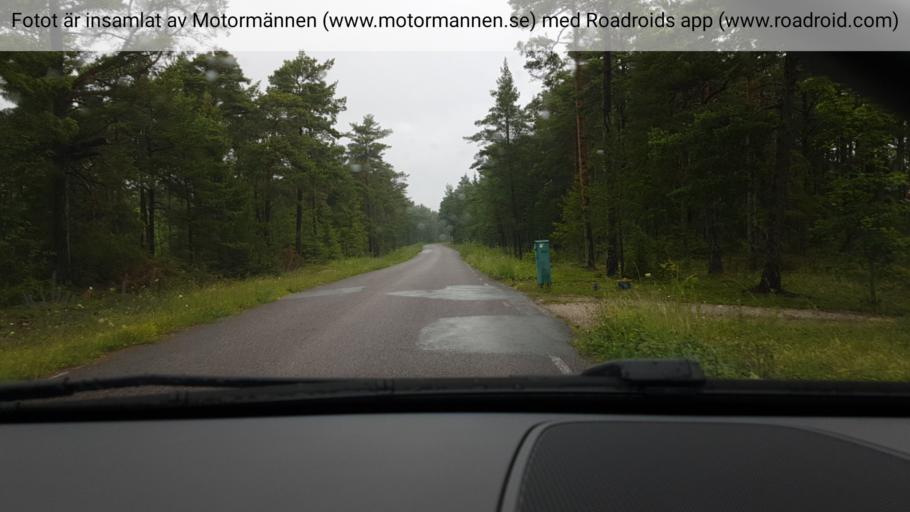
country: SE
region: Gotland
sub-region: Gotland
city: Slite
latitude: 57.8743
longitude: 18.7737
